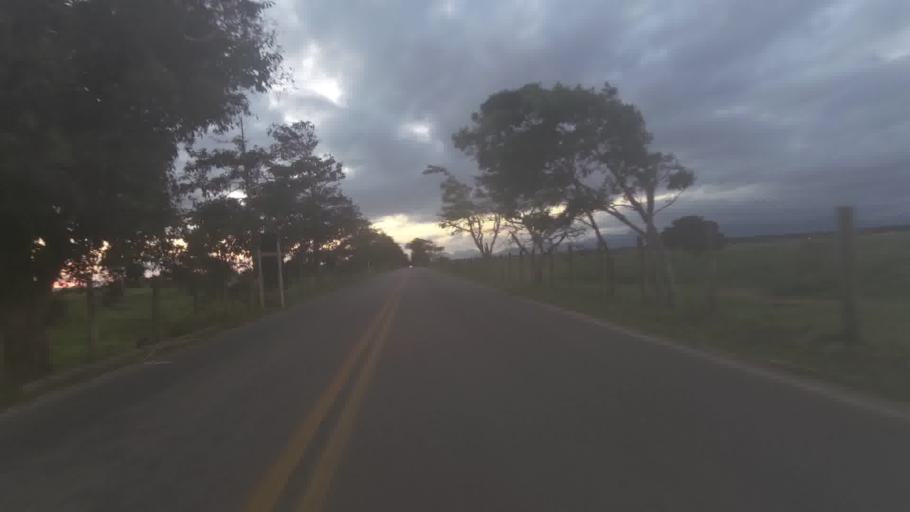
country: BR
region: Espirito Santo
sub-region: Itapemirim
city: Itapemirim
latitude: -21.0041
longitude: -40.8398
